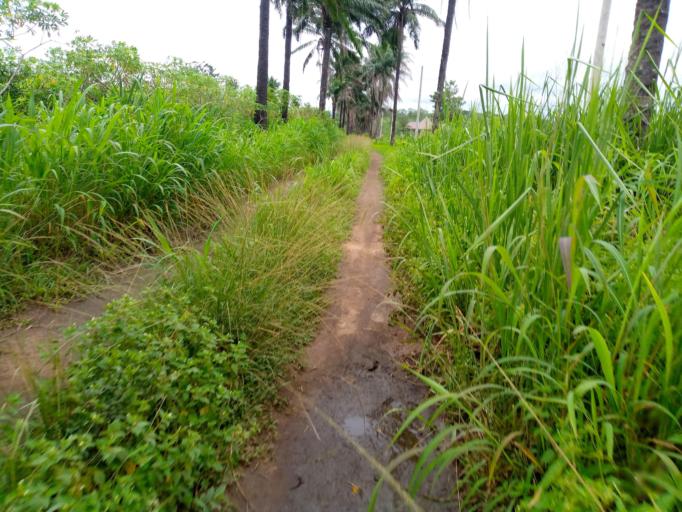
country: SL
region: Southern Province
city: Moyamba
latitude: 8.1505
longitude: -12.4427
